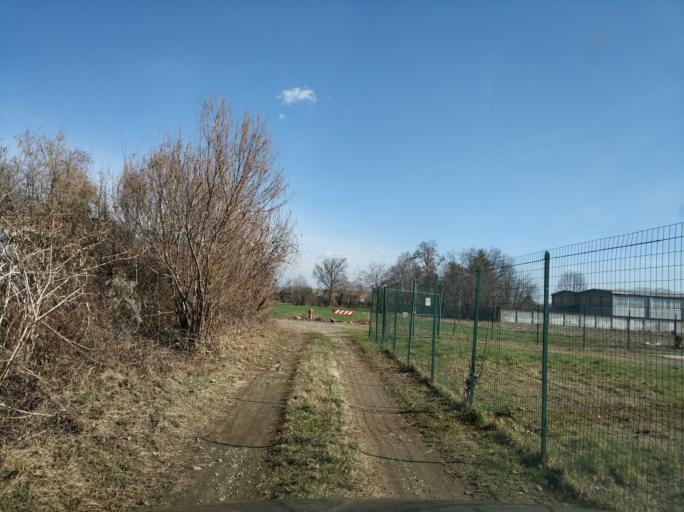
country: IT
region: Piedmont
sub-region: Provincia di Torino
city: Cirie
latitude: 45.2250
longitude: 7.6157
